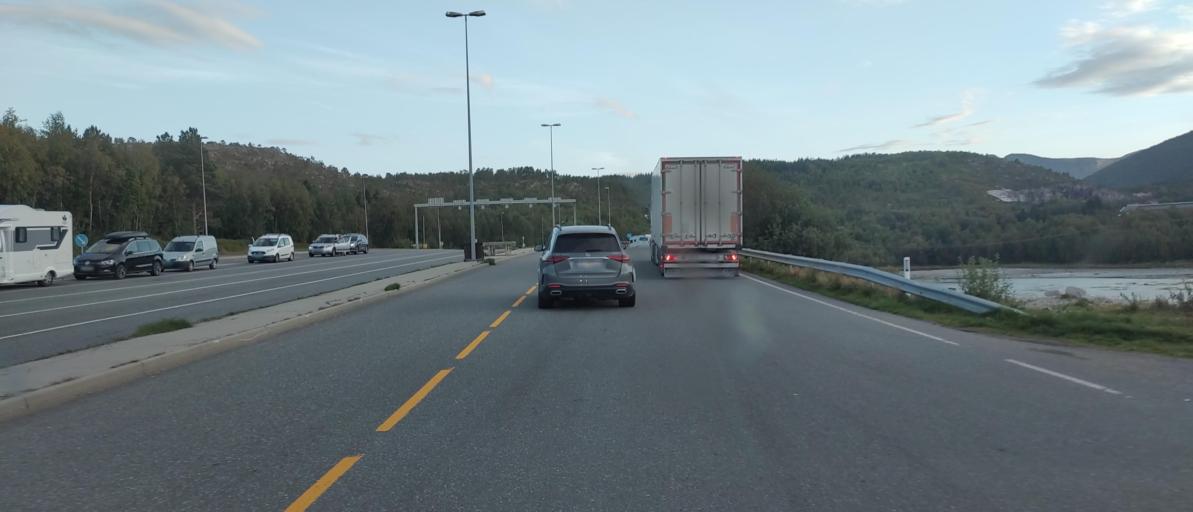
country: NO
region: Nordland
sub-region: Lodingen
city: Lodingen
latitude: 68.2232
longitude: 16.0719
